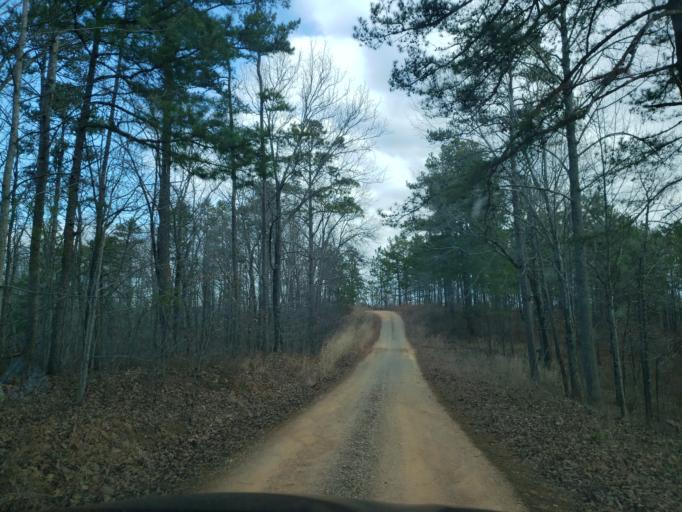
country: US
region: Alabama
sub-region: Cleburne County
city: Heflin
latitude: 33.6829
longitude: -85.6338
